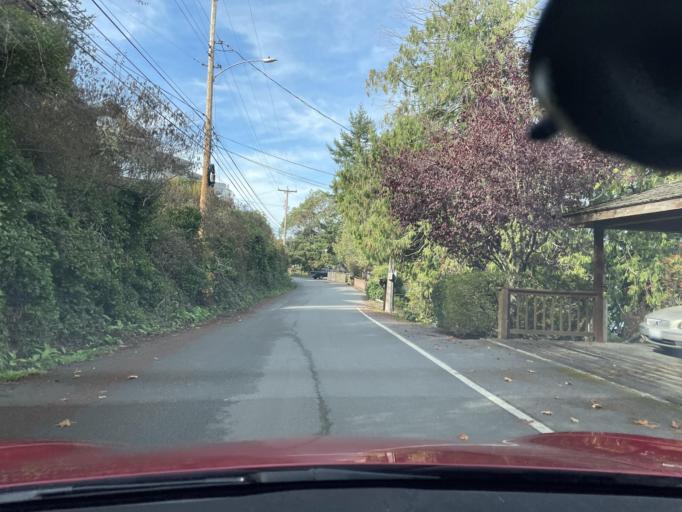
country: US
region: Washington
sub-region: San Juan County
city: Friday Harbor
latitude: 48.5342
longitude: -123.0113
